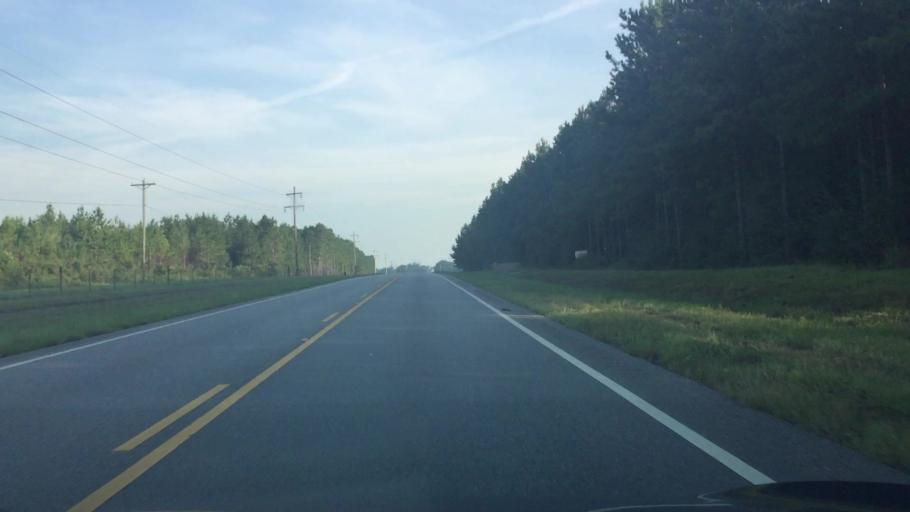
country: US
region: Alabama
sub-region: Covington County
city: Florala
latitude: 31.0402
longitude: -86.3797
